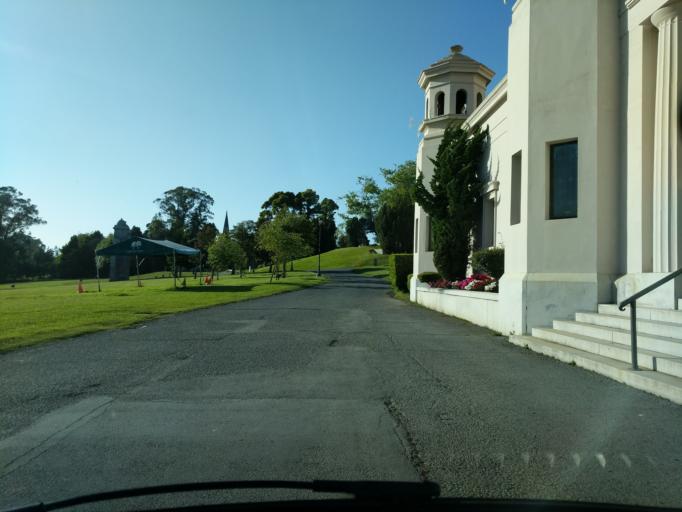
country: US
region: California
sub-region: San Mateo County
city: Colma
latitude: 37.6735
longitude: -122.4525
